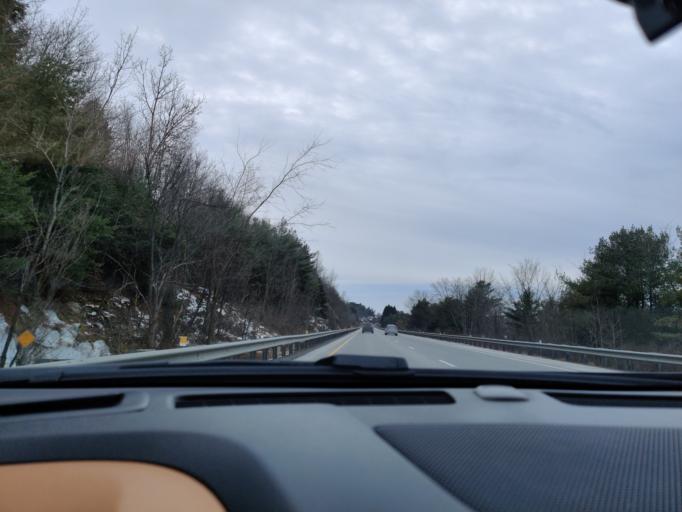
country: US
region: New York
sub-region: Jefferson County
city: Alexandria Bay
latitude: 44.4064
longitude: -75.9335
